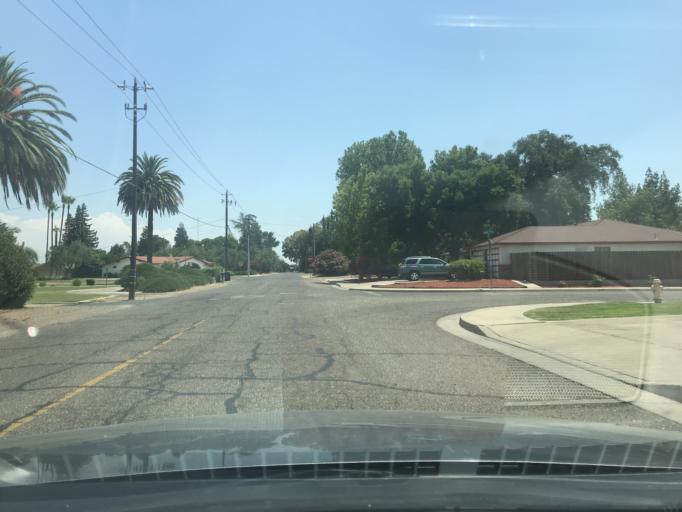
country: US
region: California
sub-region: Merced County
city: Atwater
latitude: 37.3641
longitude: -120.6086
